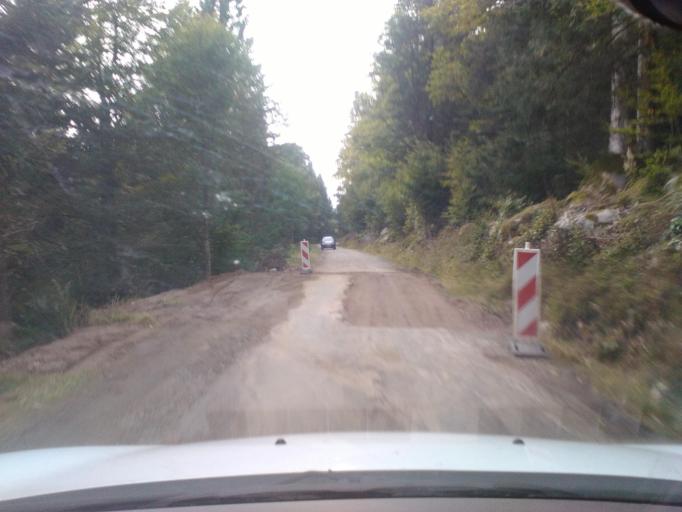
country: FR
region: Lorraine
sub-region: Departement des Vosges
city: Gerardmer
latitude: 48.0475
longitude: 6.8959
